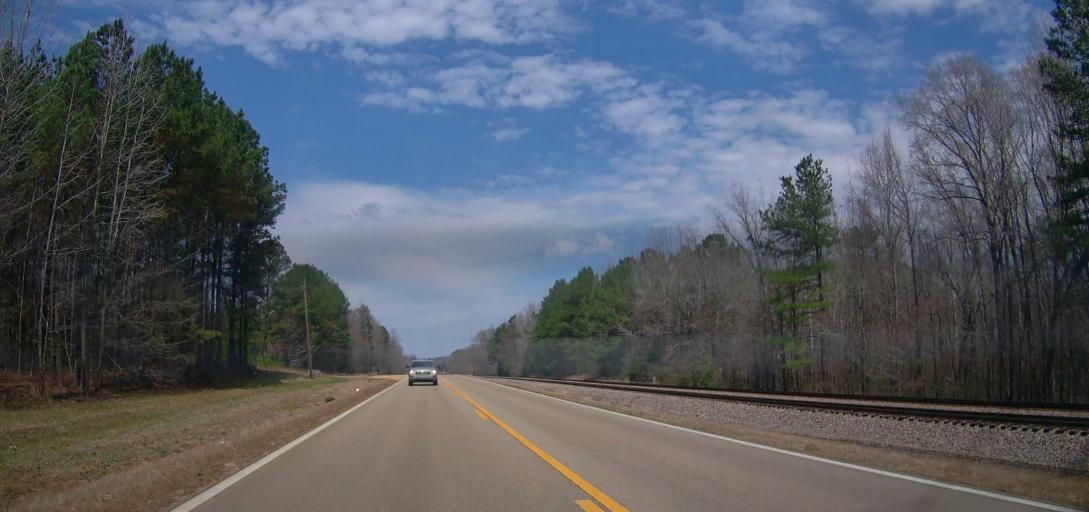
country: US
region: Mississippi
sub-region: Union County
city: New Albany
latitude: 34.5863
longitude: -89.1333
